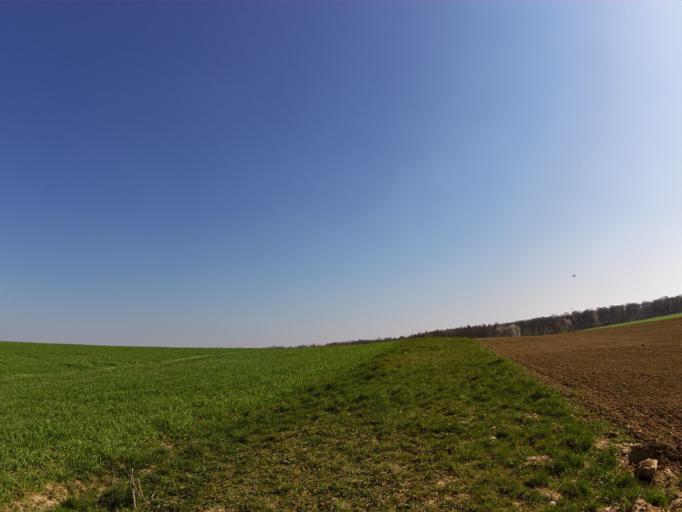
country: DE
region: Bavaria
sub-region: Regierungsbezirk Unterfranken
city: Kurnach
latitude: 49.8391
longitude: 10.0582
